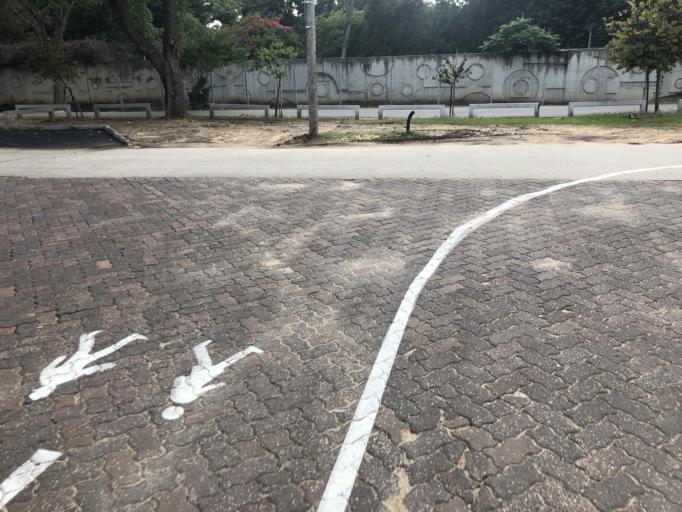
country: IL
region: Tel Aviv
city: Azor
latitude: 32.0464
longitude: 34.8233
